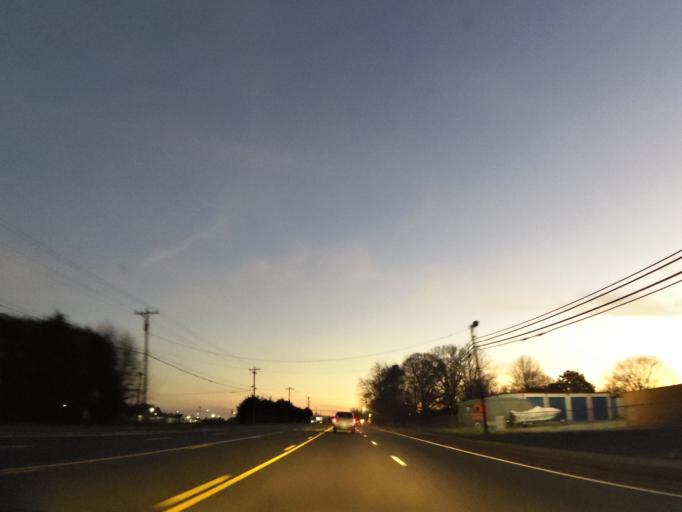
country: US
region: Georgia
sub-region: Whitfield County
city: Dalton
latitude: 34.8255
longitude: -84.9447
